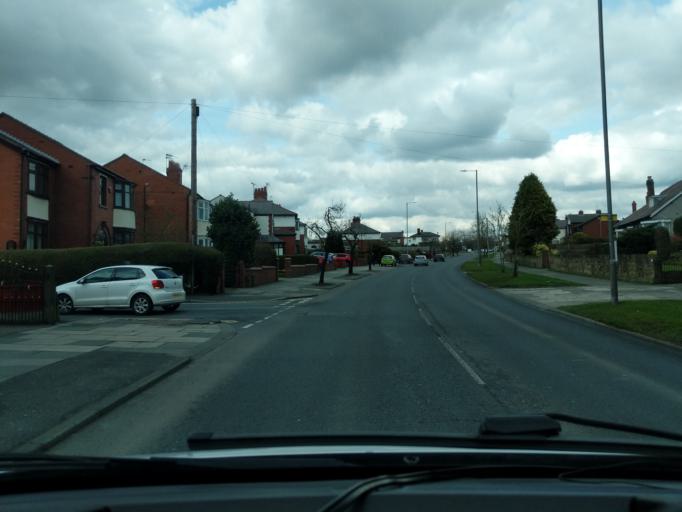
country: GB
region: England
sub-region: St. Helens
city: St Helens
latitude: 53.4692
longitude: -2.7287
